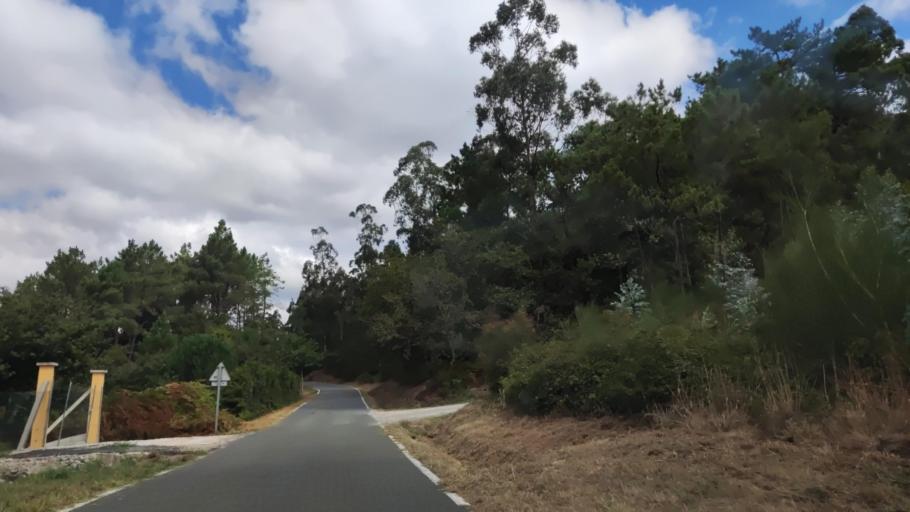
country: ES
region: Galicia
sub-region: Provincia da Coruna
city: Rois
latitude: 42.7498
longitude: -8.7016
